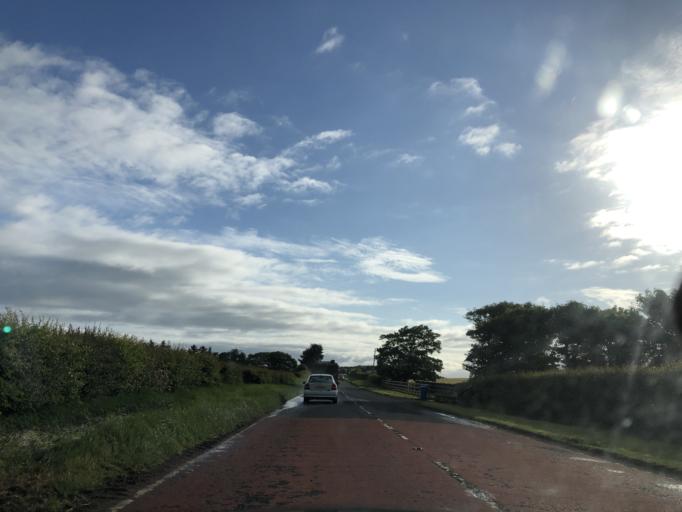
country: GB
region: Northern Ireland
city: Bushmills
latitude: 55.1863
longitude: -6.5530
